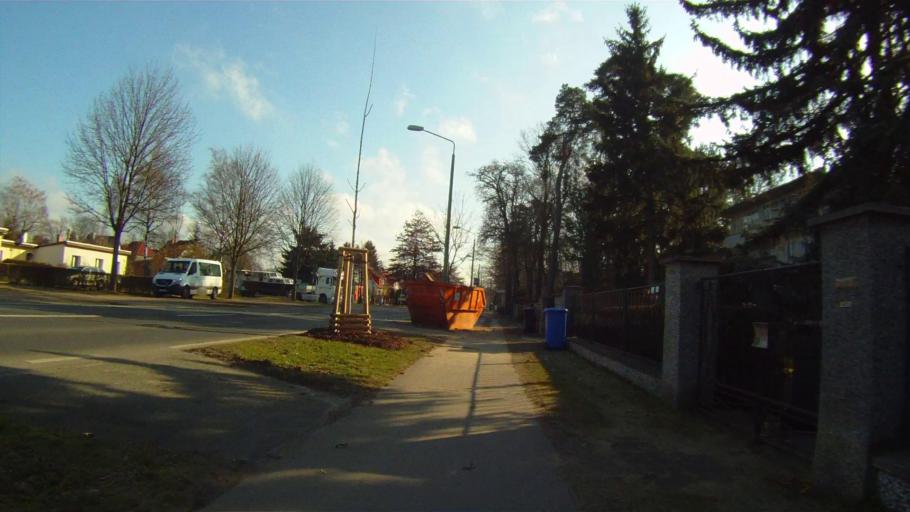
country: DE
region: Berlin
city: Rahnsdorf
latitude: 52.4327
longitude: 13.7106
